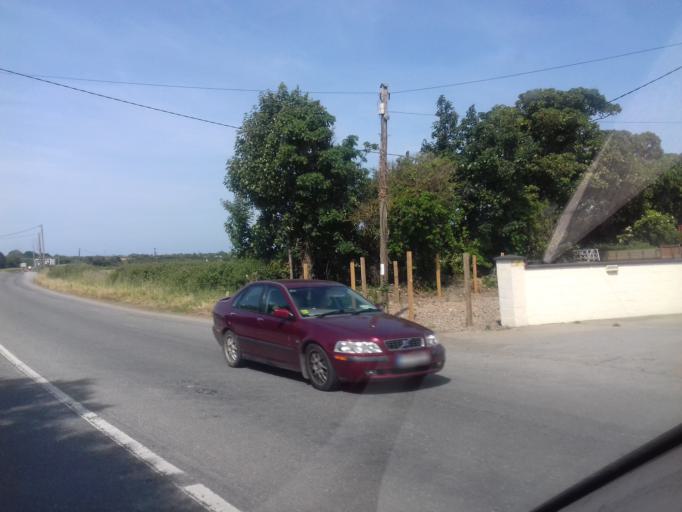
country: IE
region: Leinster
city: Lusk
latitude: 53.5234
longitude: -6.1904
